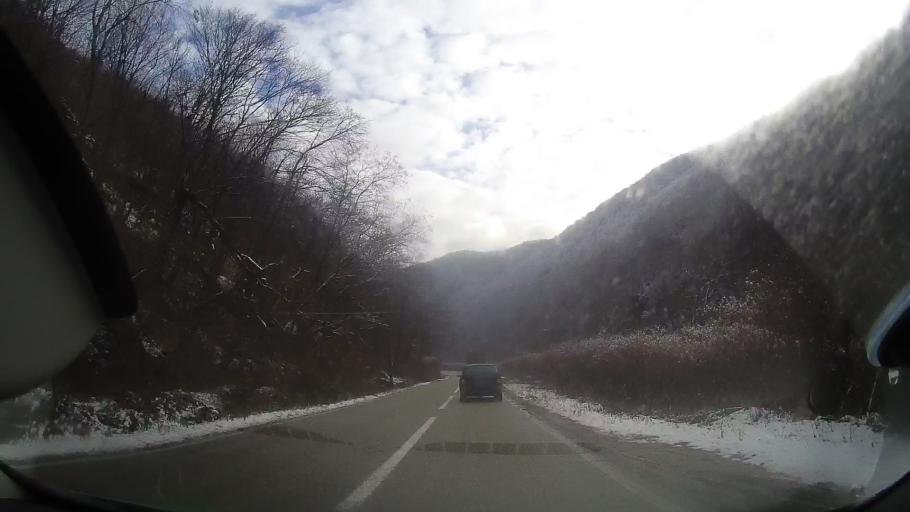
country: RO
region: Alba
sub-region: Oras Baia de Aries
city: Baia de Aries
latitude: 46.4037
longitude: 23.3418
